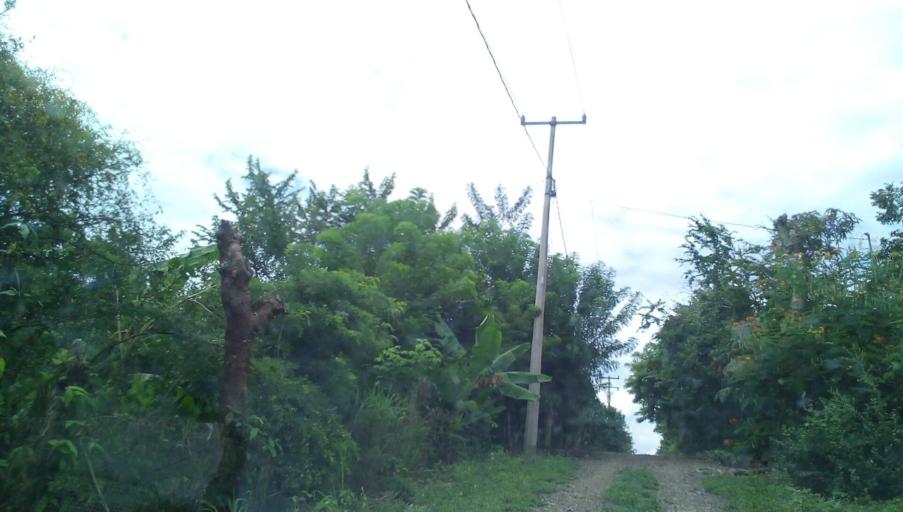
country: MX
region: Veracruz
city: Tepetzintla
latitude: 21.1248
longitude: -97.8542
